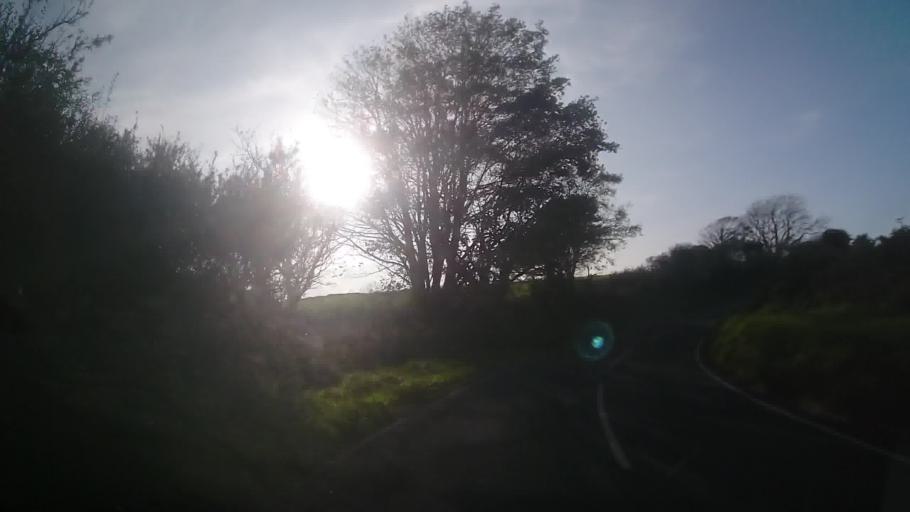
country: GB
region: Wales
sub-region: Pembrokeshire
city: Ambleston
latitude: 51.9637
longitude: -4.8953
